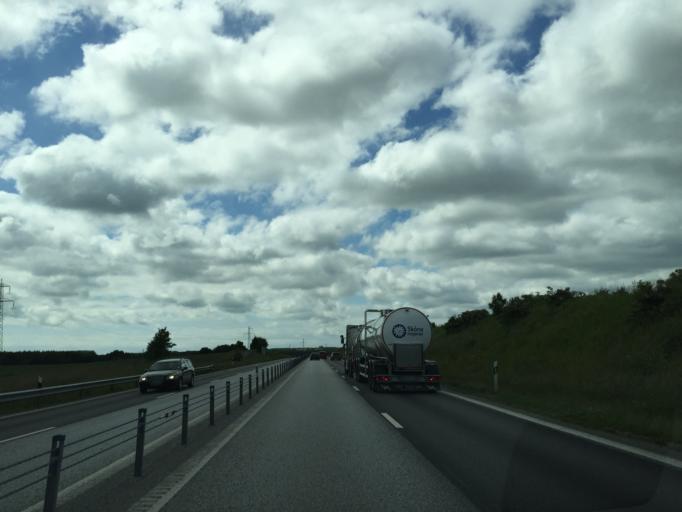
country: SE
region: Skane
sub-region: Trelleborgs Kommun
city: Anderslov
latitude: 55.5038
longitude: 13.3617
